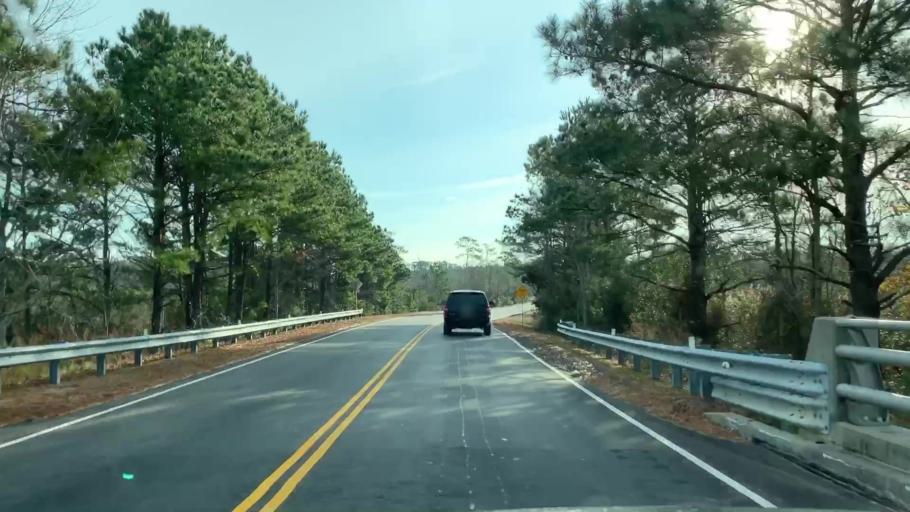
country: US
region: Virginia
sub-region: City of Virginia Beach
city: Virginia Beach
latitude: 36.6950
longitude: -76.0404
